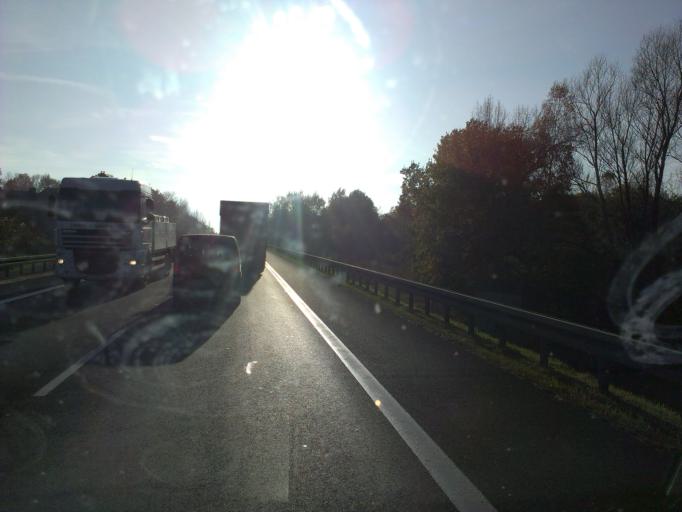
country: PL
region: Lower Silesian Voivodeship
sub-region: Legnica
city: Legnica
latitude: 51.2066
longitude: 16.1201
